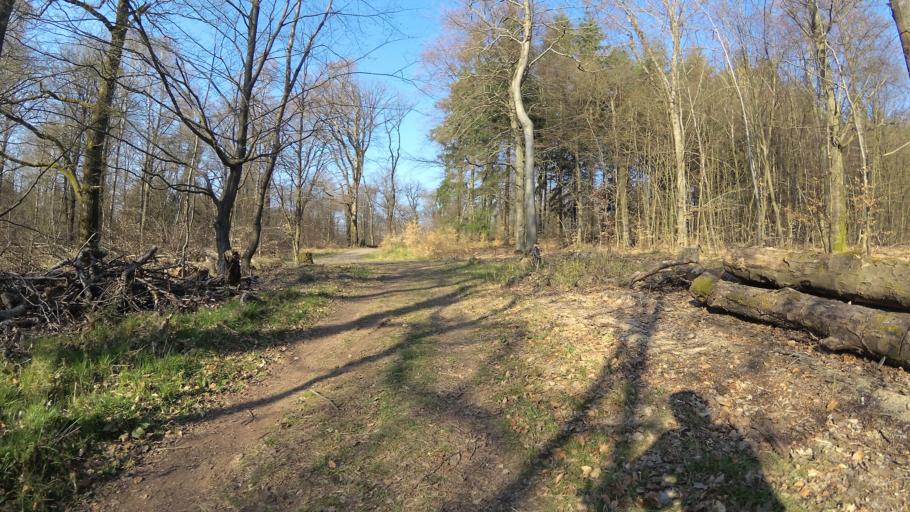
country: DE
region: Saarland
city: Ottweiler
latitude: 49.3896
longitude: 7.1549
